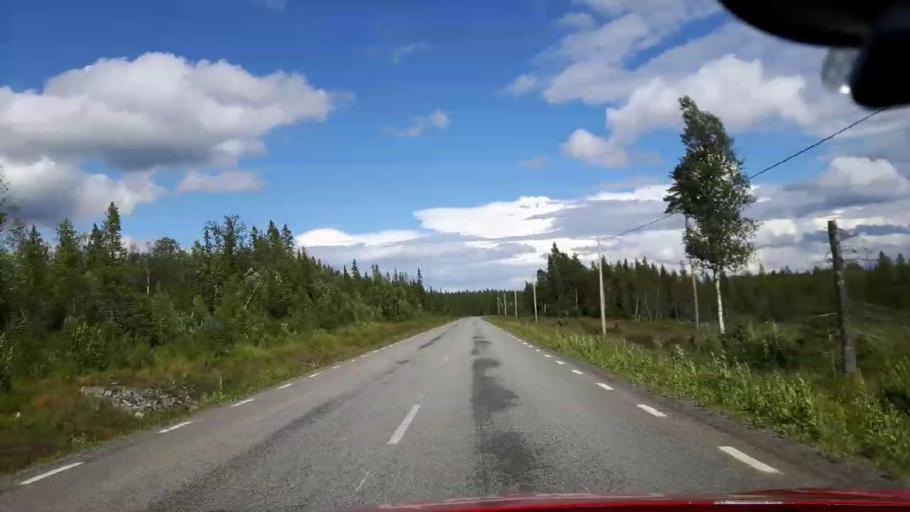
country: SE
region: Jaemtland
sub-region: Are Kommun
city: Are
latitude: 63.2187
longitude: 13.0902
